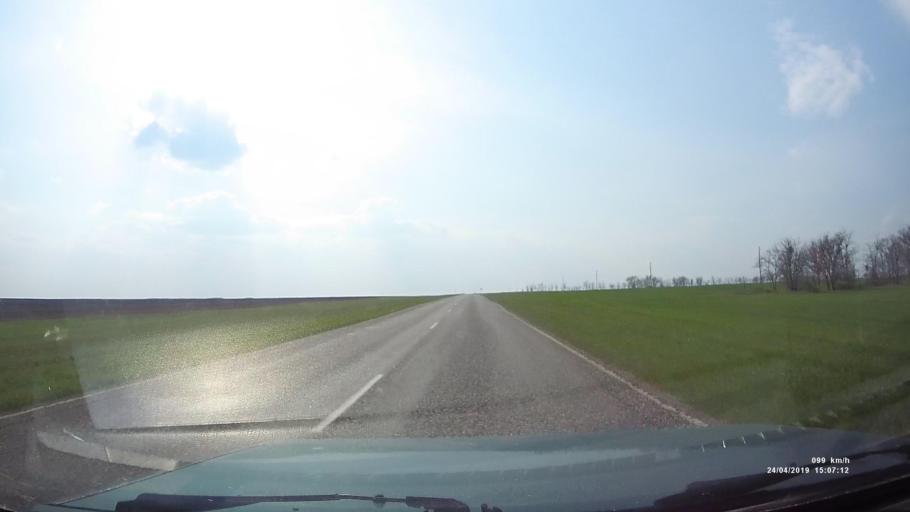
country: RU
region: Rostov
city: Remontnoye
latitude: 46.5594
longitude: 43.4099
